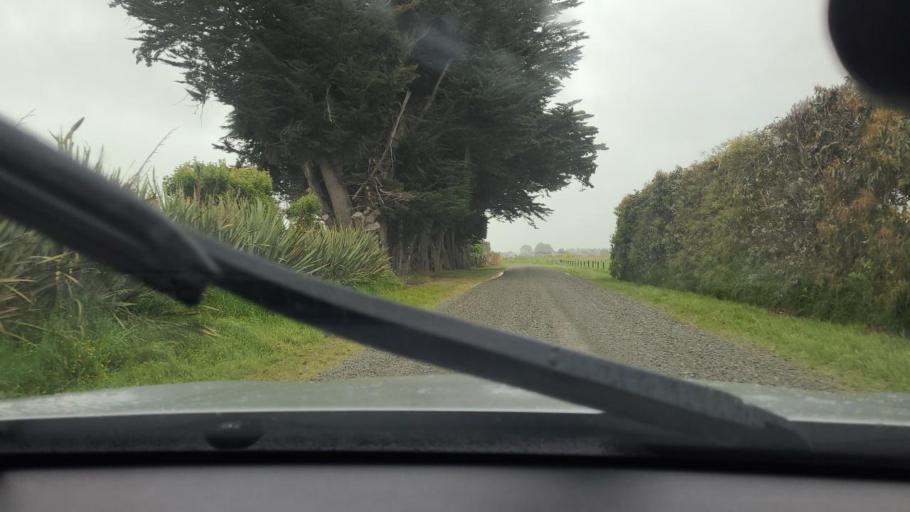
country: NZ
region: Southland
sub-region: Southland District
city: Winton
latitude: -46.1550
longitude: 168.3347
